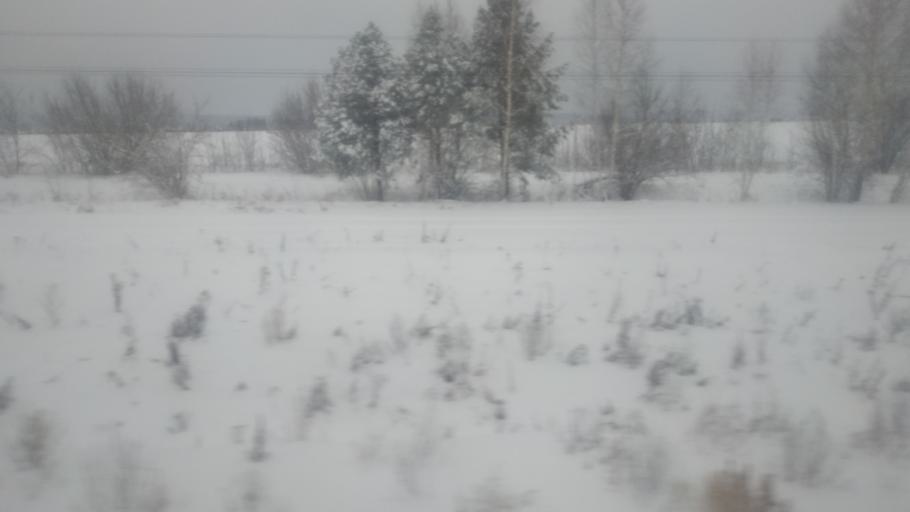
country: RU
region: Bashkortostan
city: Amzya
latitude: 56.2485
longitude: 54.6504
